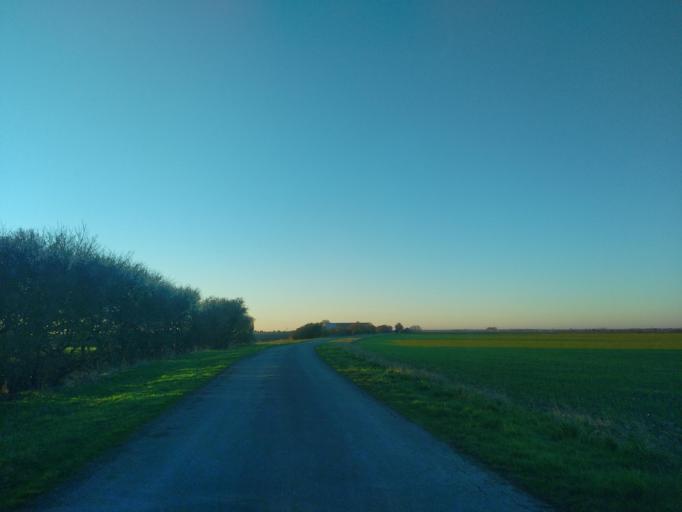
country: FR
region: Pays de la Loire
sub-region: Departement de la Vendee
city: Triaize
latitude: 46.3742
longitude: -1.2879
